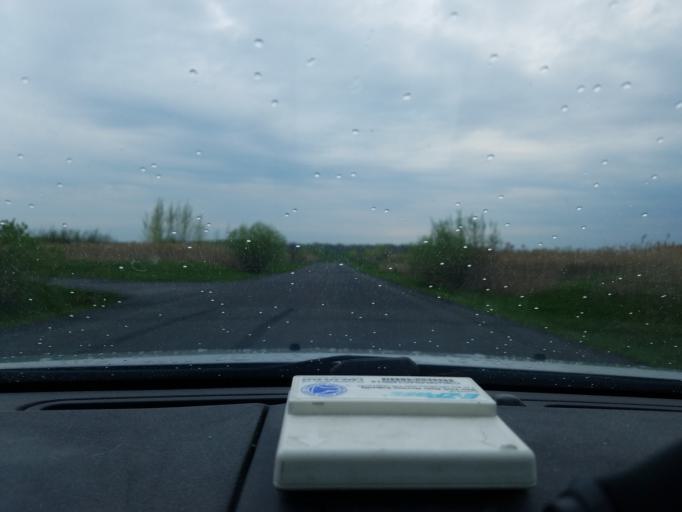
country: US
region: New York
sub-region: Onondaga County
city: East Syracuse
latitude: 43.1048
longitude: -76.0875
